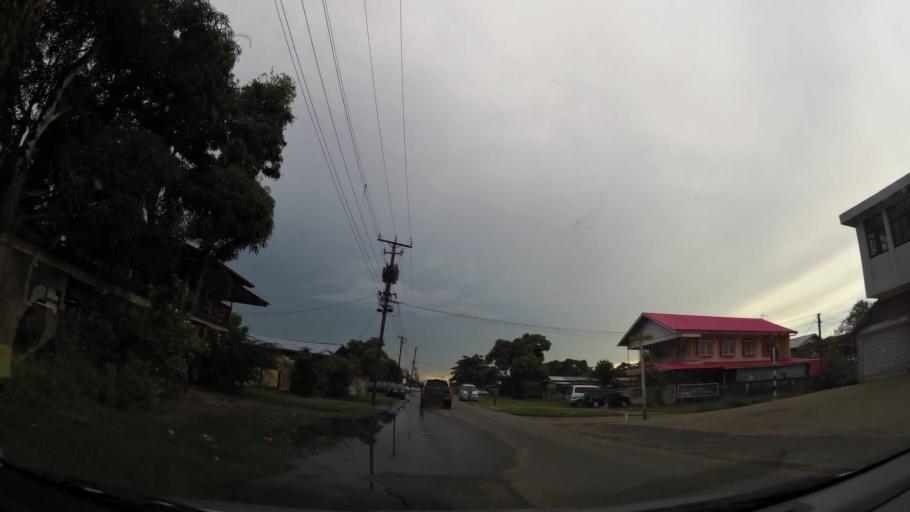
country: SR
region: Paramaribo
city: Paramaribo
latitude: 5.8101
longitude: -55.1982
